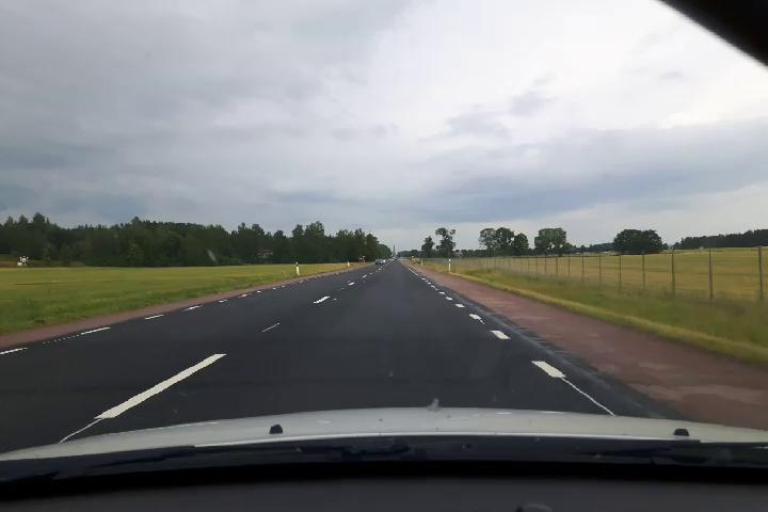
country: SE
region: Uppsala
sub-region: Uppsala Kommun
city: Gamla Uppsala
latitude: 59.8905
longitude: 17.6170
